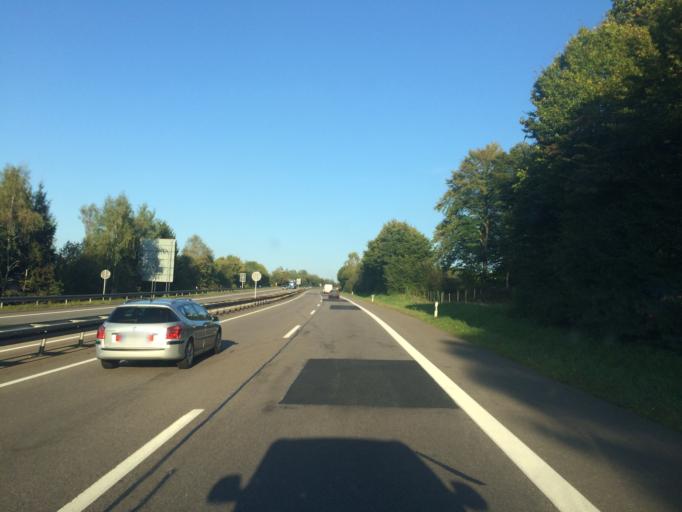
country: DE
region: Saarland
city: Eppelborn
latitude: 49.4126
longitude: 6.9976
